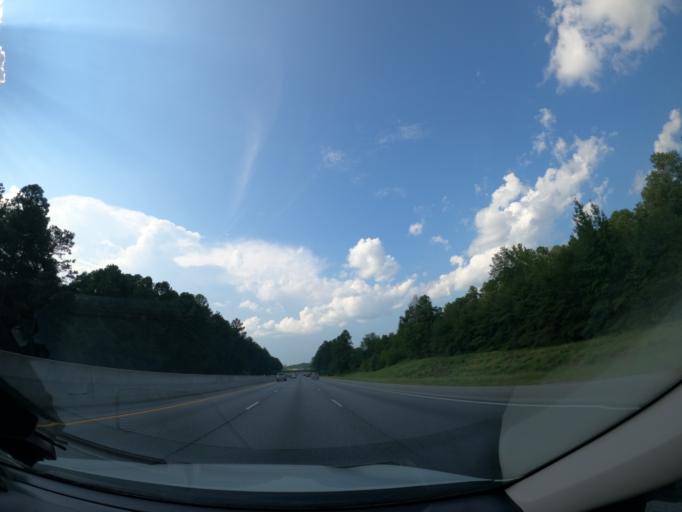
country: US
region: Georgia
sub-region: Columbia County
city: Martinez
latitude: 33.4415
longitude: -82.0723
